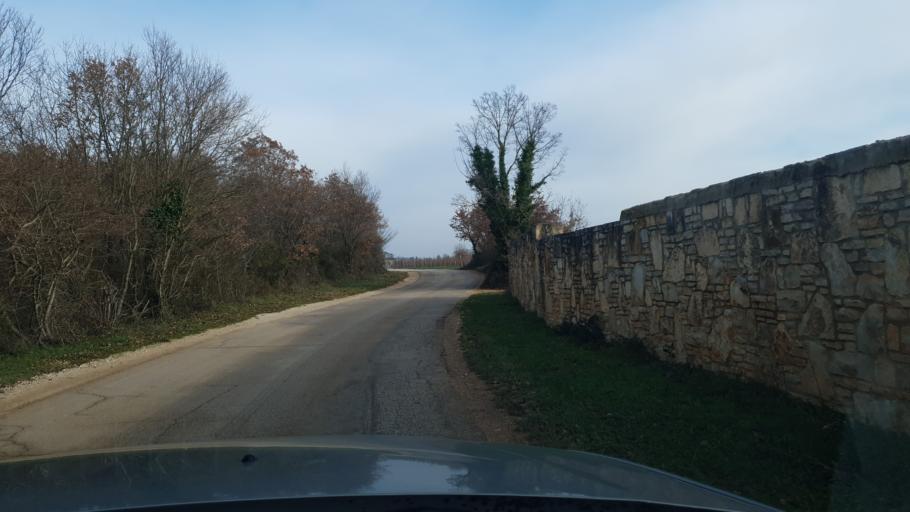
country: HR
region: Istarska
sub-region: Grad Porec
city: Porec
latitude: 45.2420
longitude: 13.6534
